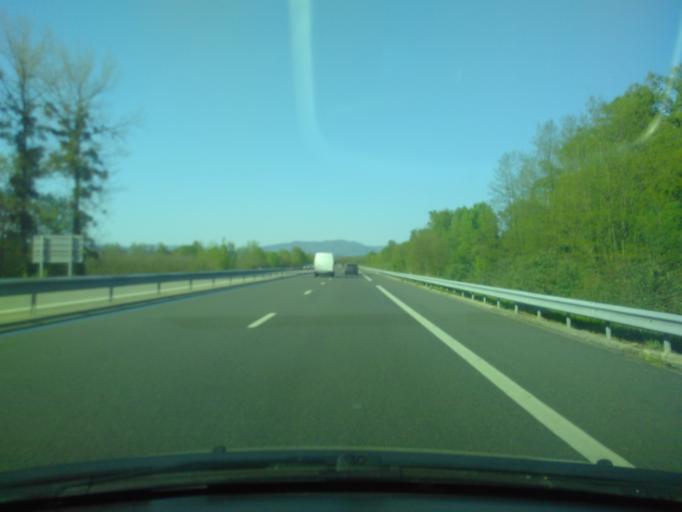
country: FR
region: Rhone-Alpes
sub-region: Departement de l'Isere
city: Saint-Quentin-sur-Isere
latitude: 45.2751
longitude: 5.5219
